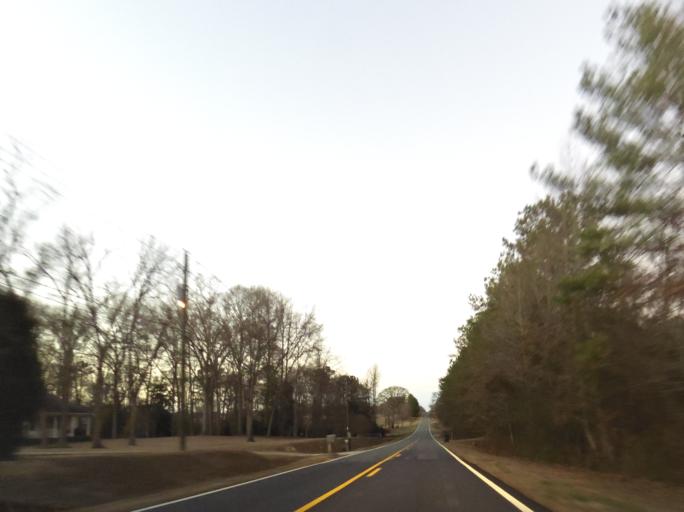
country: US
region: Georgia
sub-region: Peach County
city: Byron
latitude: 32.6247
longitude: -83.7574
